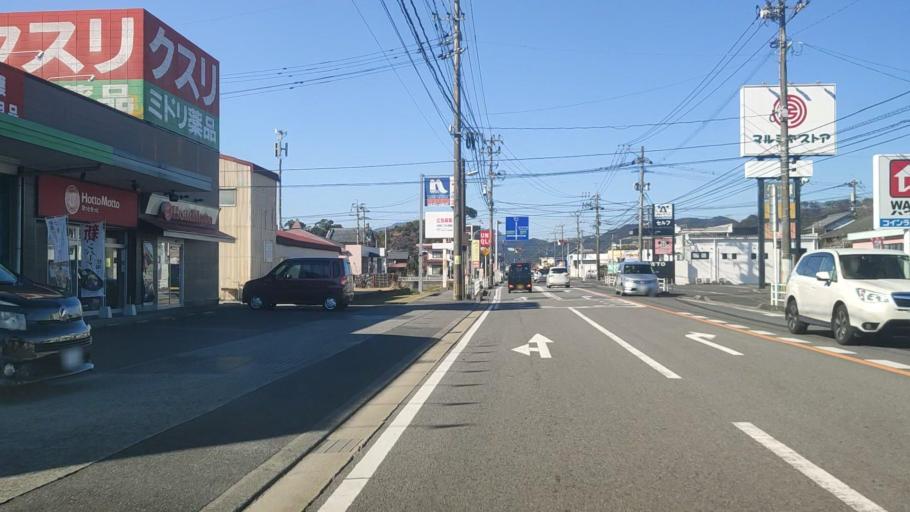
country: JP
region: Oita
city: Saiki
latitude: 32.9457
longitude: 131.9025
